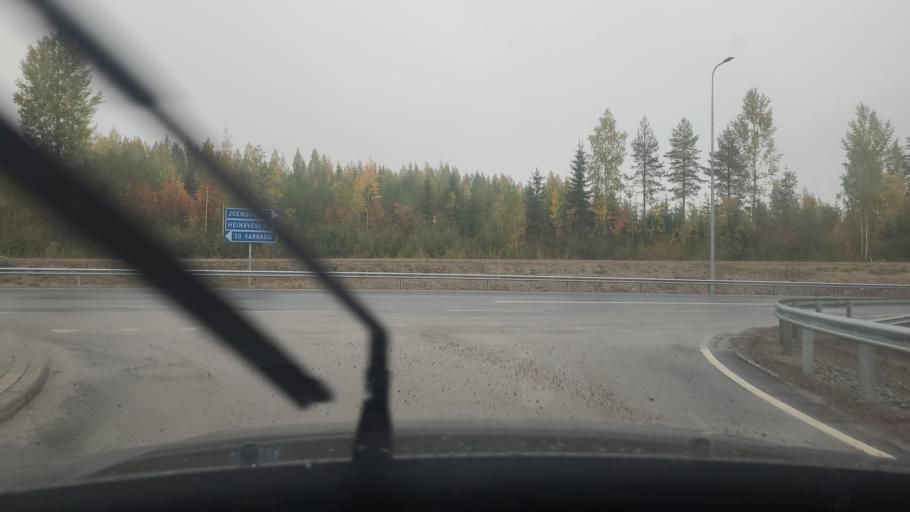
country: FI
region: Northern Savo
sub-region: Varkaus
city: Kangaslampi
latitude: 62.4539
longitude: 28.2863
